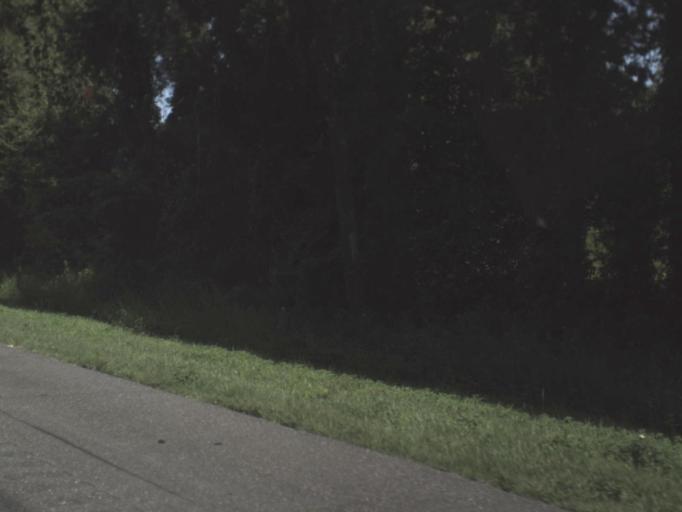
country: US
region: Florida
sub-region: Suwannee County
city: Wellborn
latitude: 30.2911
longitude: -82.8716
